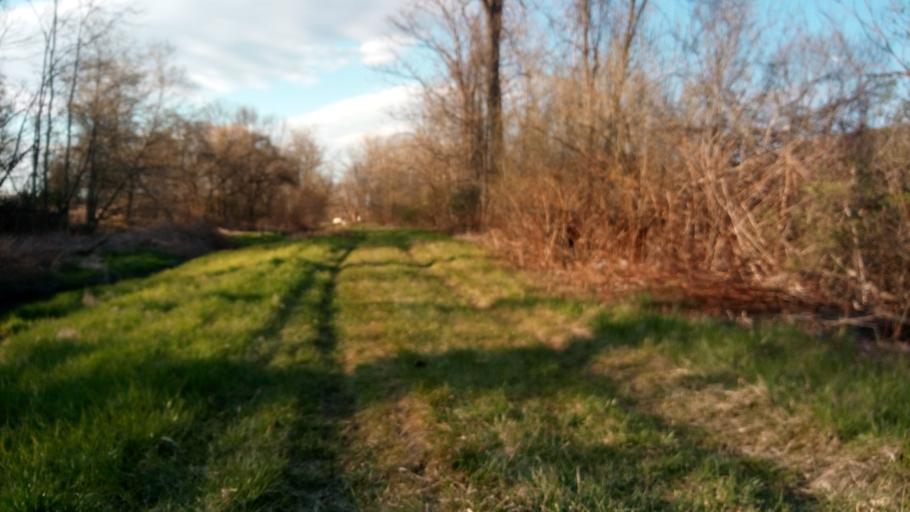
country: US
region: New York
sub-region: Chemung County
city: Elmira Heights
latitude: 42.1198
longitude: -76.8109
